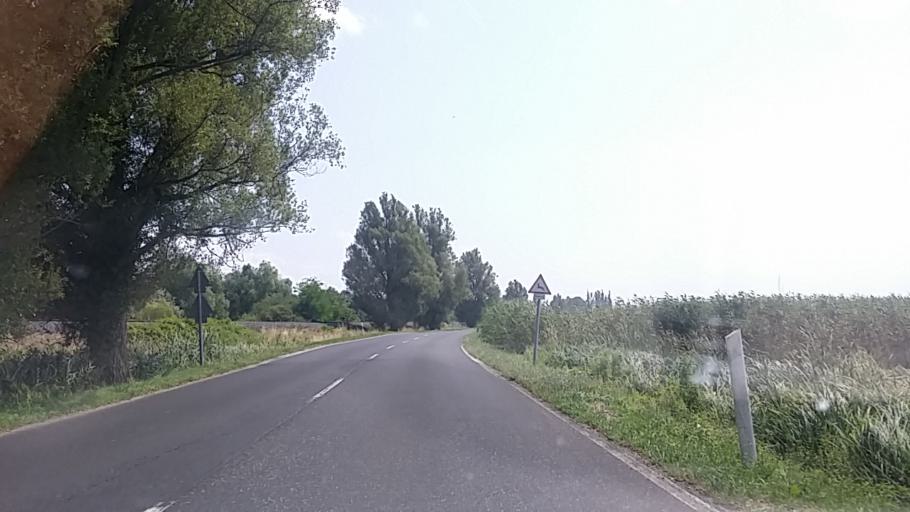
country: HU
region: Veszprem
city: Badacsonytomaj
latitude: 46.8045
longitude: 17.4681
